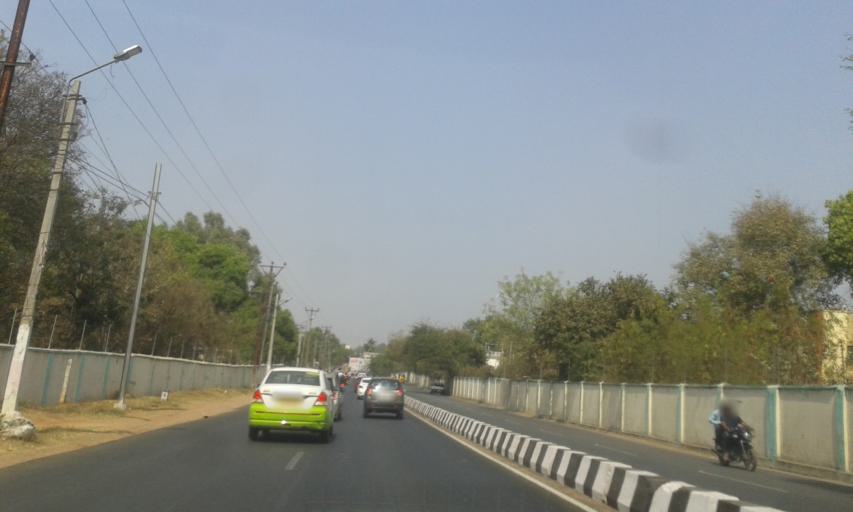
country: IN
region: Telangana
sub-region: Rangareddi
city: Secunderabad
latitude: 17.4882
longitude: 78.5122
